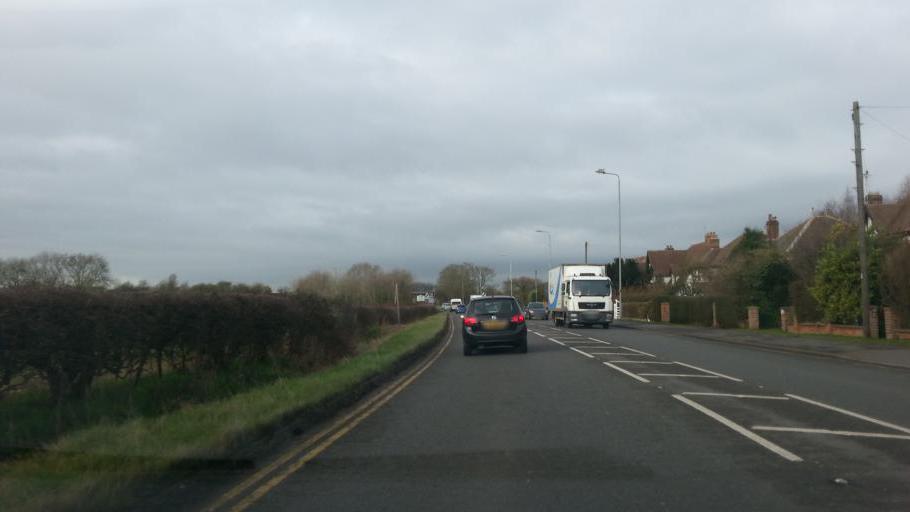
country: GB
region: England
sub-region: Nottinghamshire
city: West Bridgford
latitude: 52.9005
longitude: -1.1042
